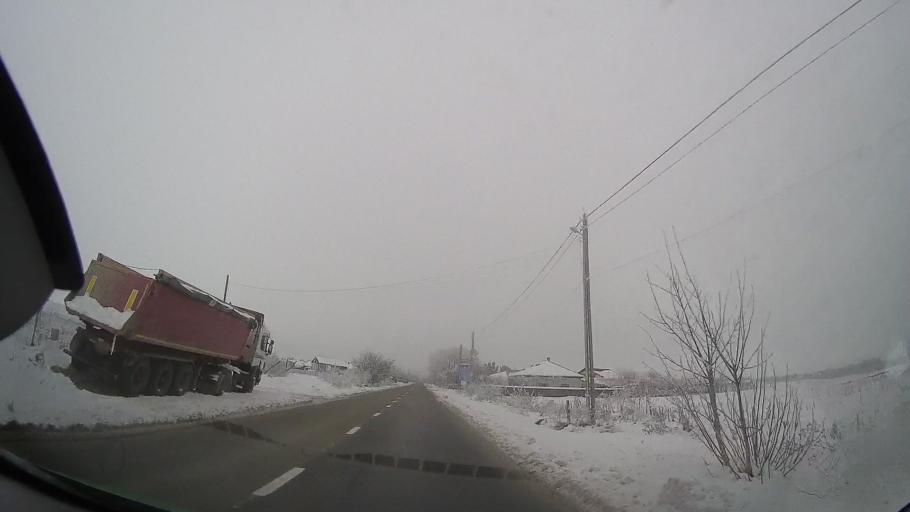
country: RO
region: Neamt
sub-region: Comuna Horia
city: Cotu Vames
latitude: 46.8955
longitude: 26.9604
